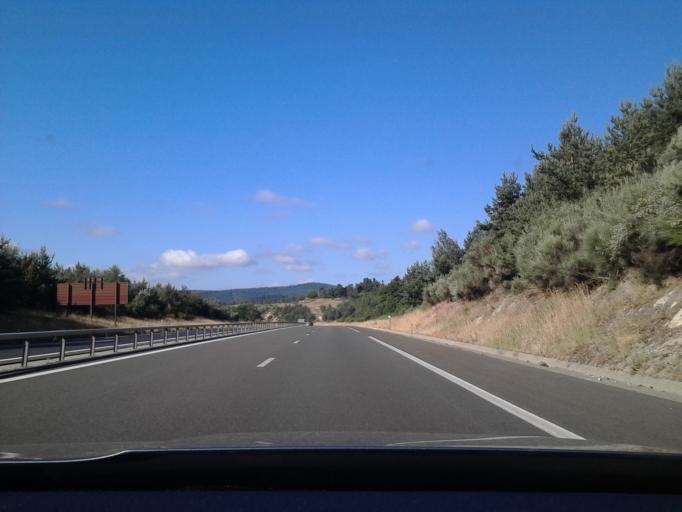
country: FR
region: Languedoc-Roussillon
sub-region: Departement de la Lozere
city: Aumont-Aubrac
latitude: 44.6489
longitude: 3.2466
